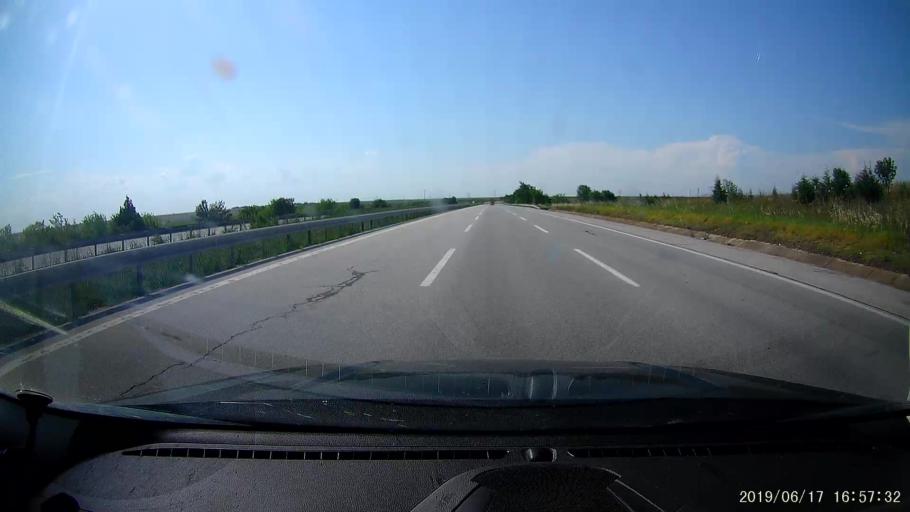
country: TR
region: Edirne
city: Haskoy
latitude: 41.6024
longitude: 26.9119
